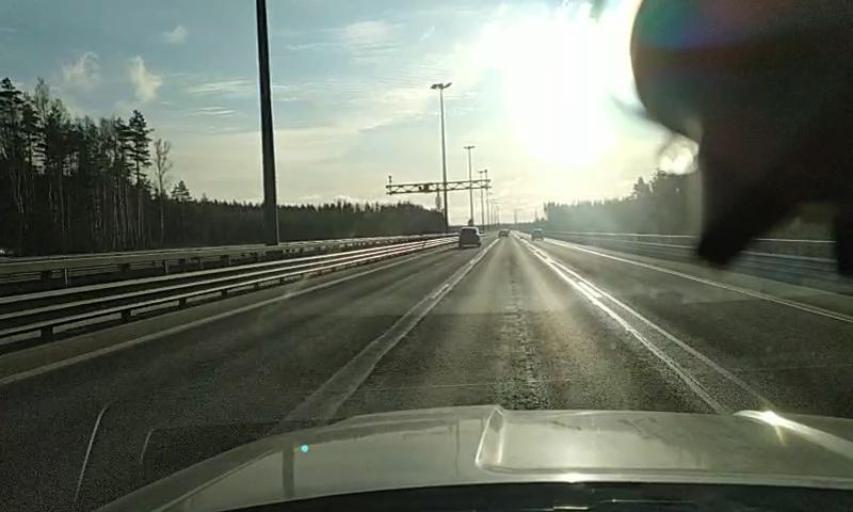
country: RU
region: St.-Petersburg
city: Pesochnyy
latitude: 60.0950
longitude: 30.0949
